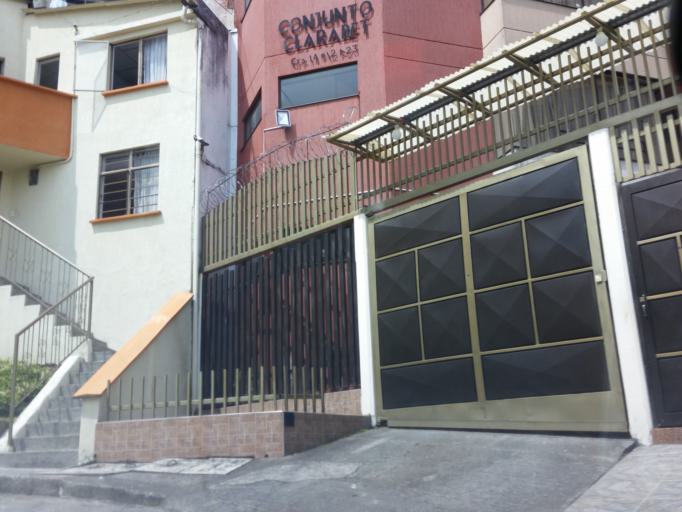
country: CO
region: Caldas
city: Manizales
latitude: 5.0725
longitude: -75.5239
